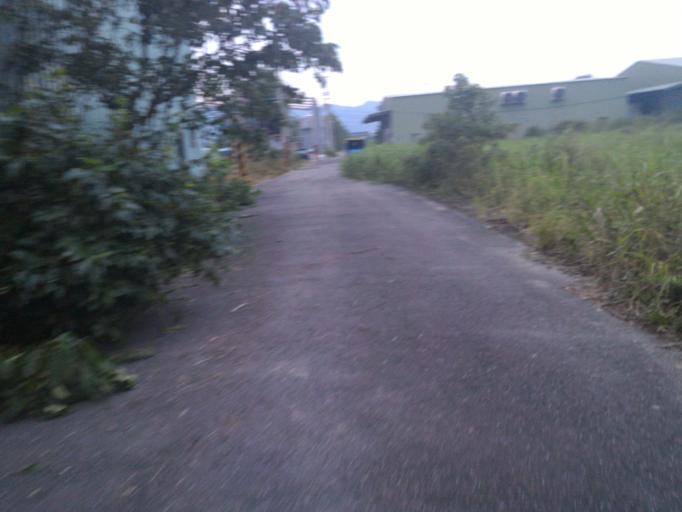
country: TW
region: Taiwan
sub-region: Taoyuan
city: Taoyuan
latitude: 24.9522
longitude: 121.3984
